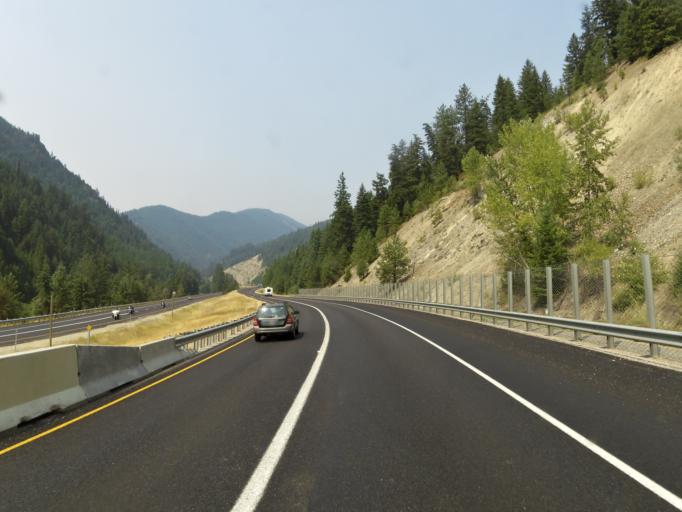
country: US
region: Montana
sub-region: Sanders County
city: Thompson Falls
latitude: 47.3123
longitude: -115.2112
